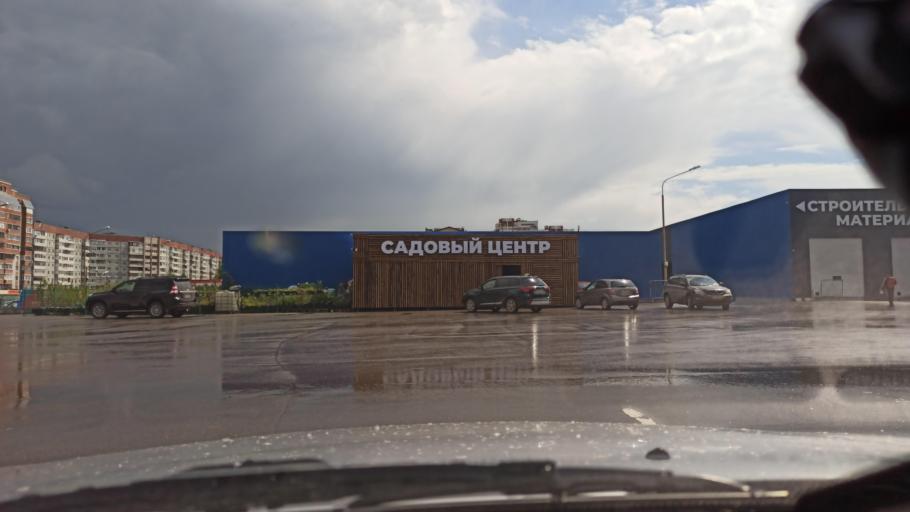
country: RU
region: Vologda
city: Vologda
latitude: 59.1990
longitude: 39.8203
